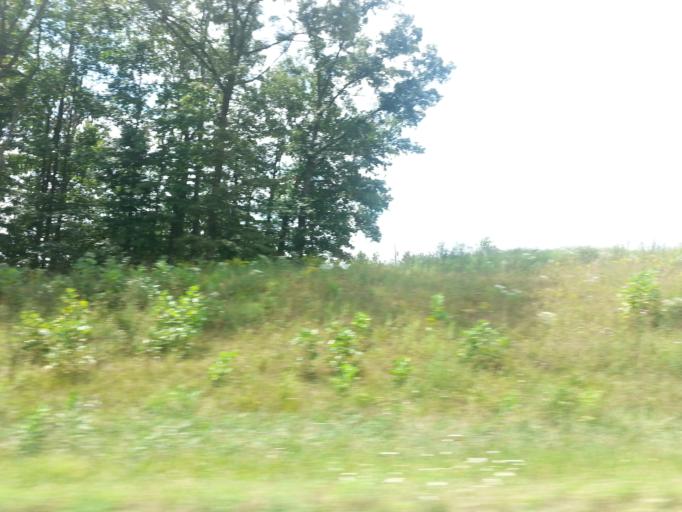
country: US
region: Tennessee
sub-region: Cumberland County
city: Crossville
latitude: 36.0239
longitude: -85.0825
